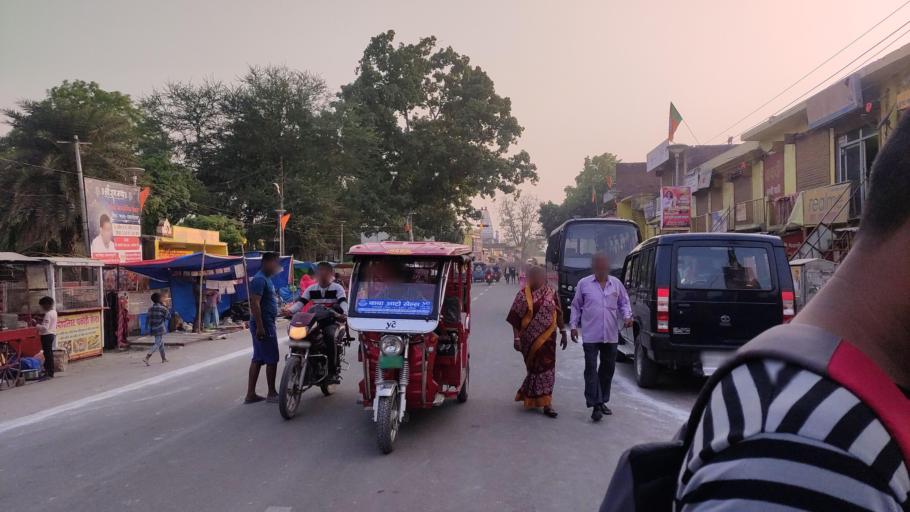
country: IN
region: Uttar Pradesh
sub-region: Faizabad
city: Ayodhya
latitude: 26.7929
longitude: 82.2004
